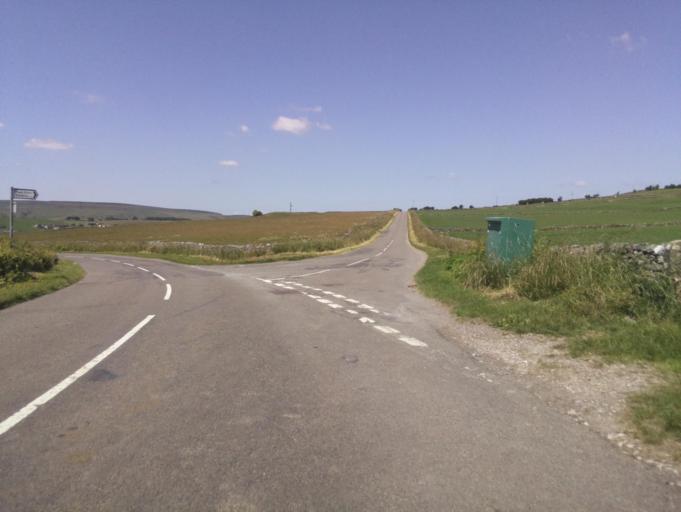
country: GB
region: England
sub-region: Derbyshire
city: Buxton
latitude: 53.2794
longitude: -1.8470
